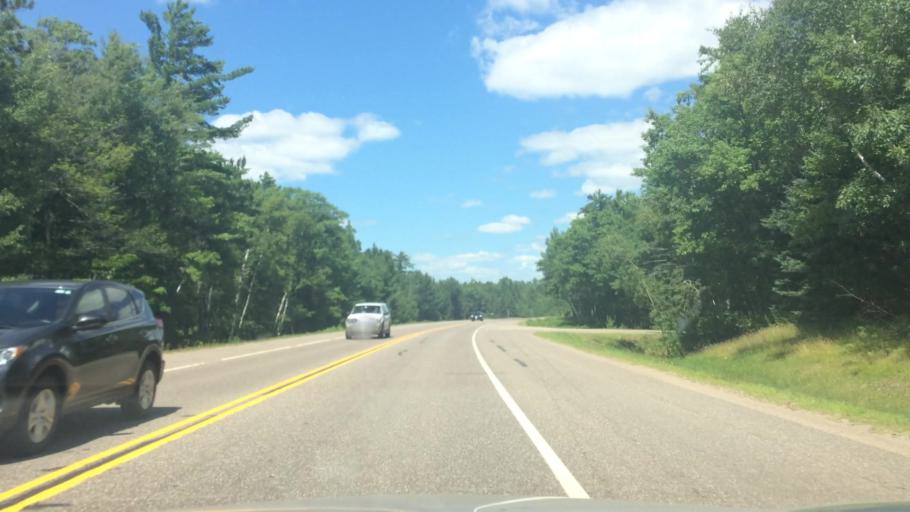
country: US
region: Wisconsin
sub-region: Vilas County
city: Lac du Flambeau
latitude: 45.9469
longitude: -89.6998
